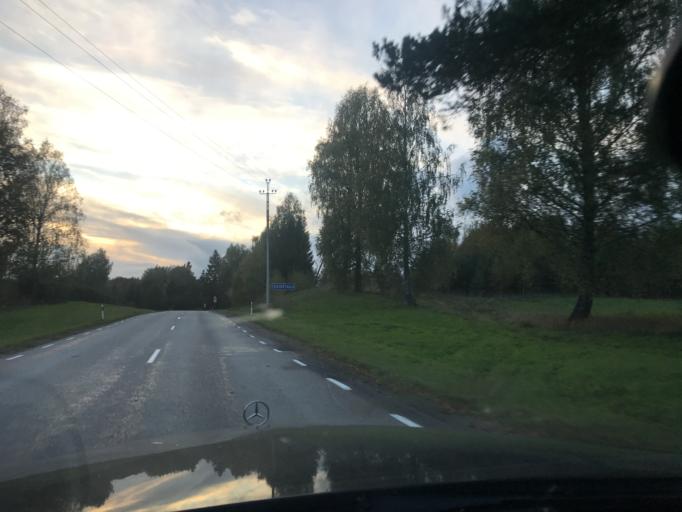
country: EE
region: Valgamaa
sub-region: Torva linn
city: Torva
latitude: 58.0072
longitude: 26.0917
